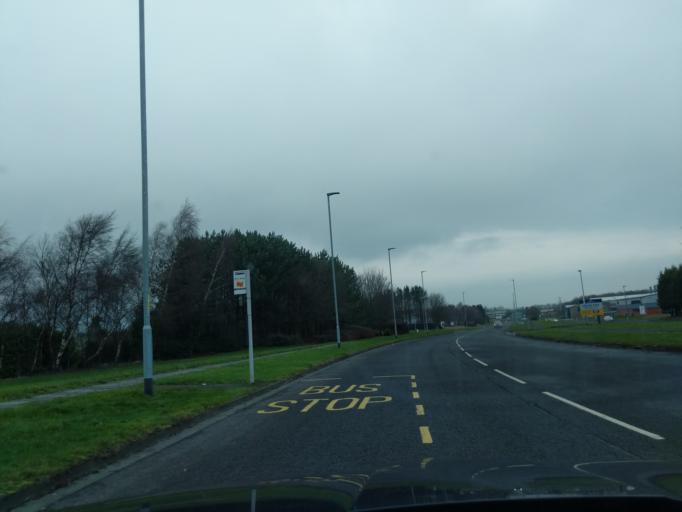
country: GB
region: England
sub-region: Northumberland
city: Cramlington
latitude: 55.0968
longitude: -1.6099
